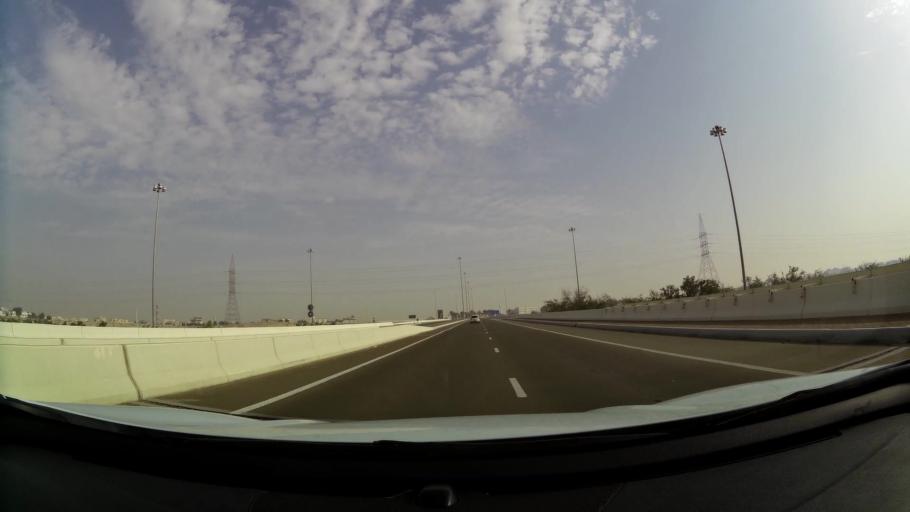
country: AE
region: Abu Dhabi
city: Abu Dhabi
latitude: 24.2519
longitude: 54.7083
